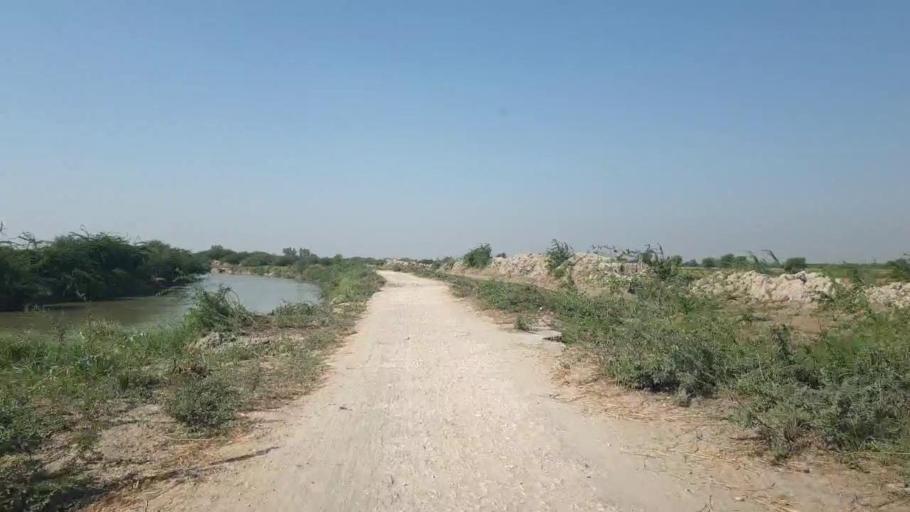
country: PK
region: Sindh
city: Talhar
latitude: 24.8299
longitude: 68.7880
